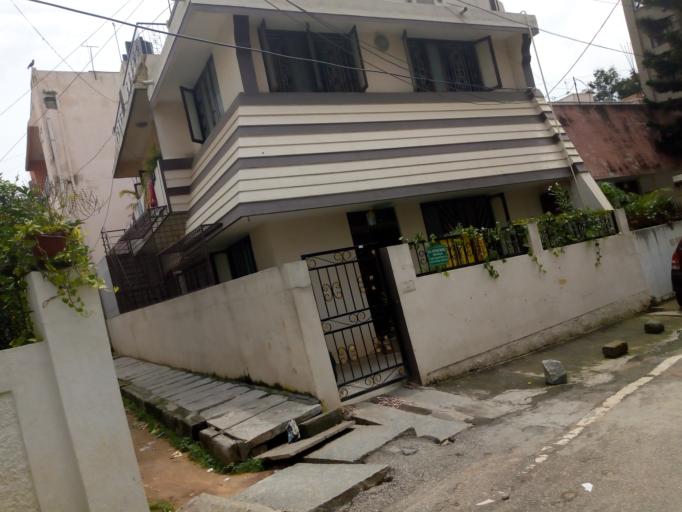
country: IN
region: Karnataka
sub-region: Bangalore Urban
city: Bangalore
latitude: 12.9735
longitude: 77.6480
